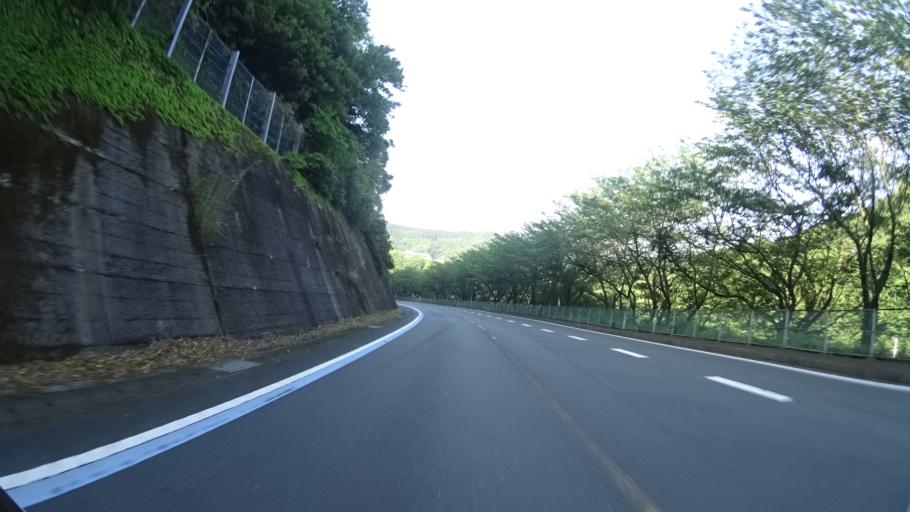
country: JP
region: Ehime
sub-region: Nishiuwa-gun
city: Ikata-cho
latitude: 33.3889
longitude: 132.1338
